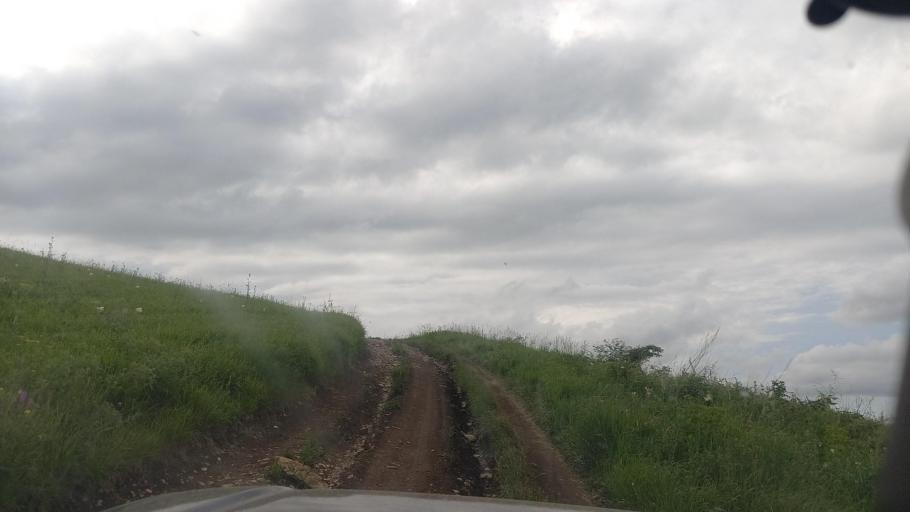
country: RU
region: Krasnodarskiy
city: Peredovaya
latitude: 44.0553
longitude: 41.3654
